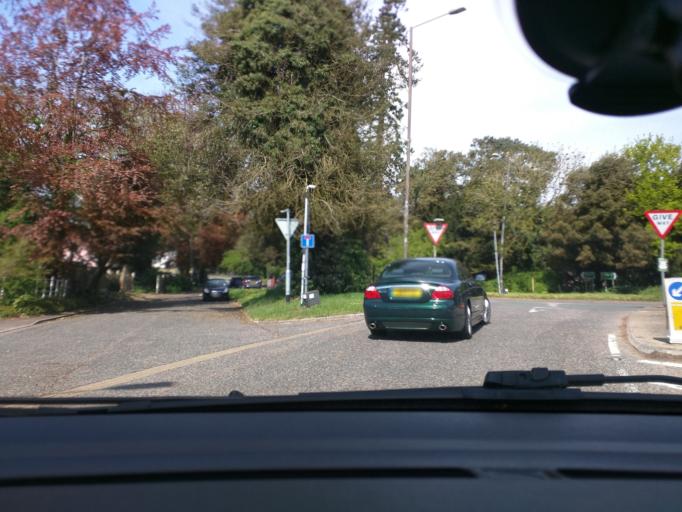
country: GB
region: England
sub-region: Suffolk
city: Saxmundham
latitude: 52.2642
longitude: 1.5139
